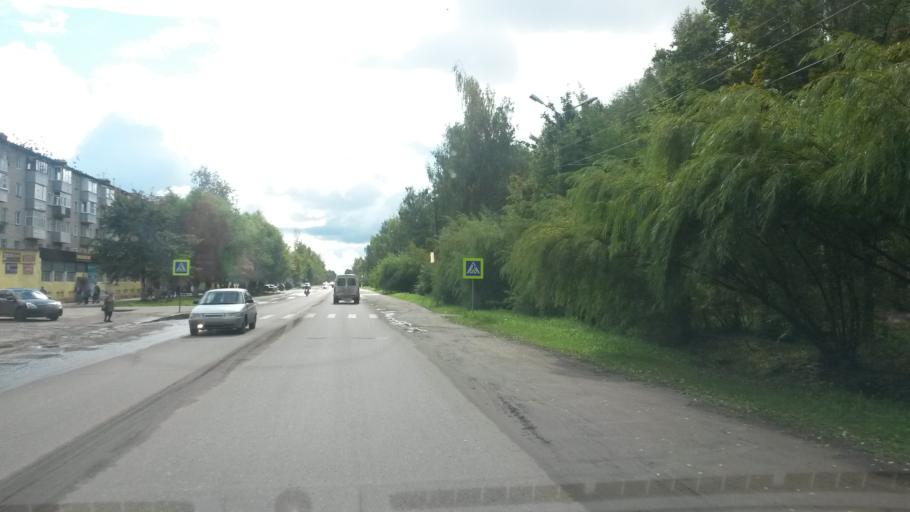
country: RU
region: Ivanovo
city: Zavolzhsk
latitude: 57.4888
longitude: 42.1404
